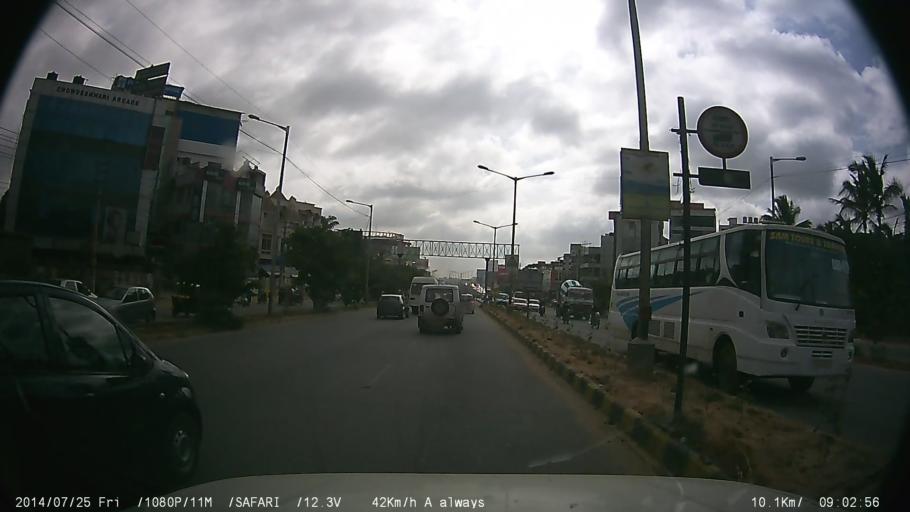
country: IN
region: Karnataka
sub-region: Bangalore Urban
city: Bangalore
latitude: 12.9241
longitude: 77.6725
